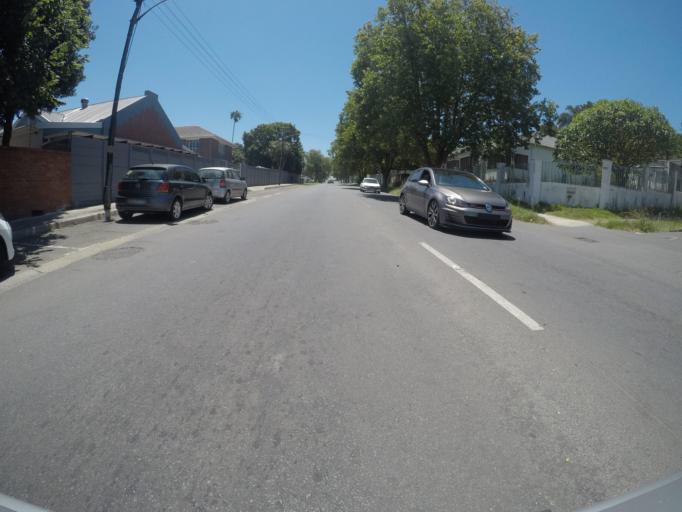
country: ZA
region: Eastern Cape
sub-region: Buffalo City Metropolitan Municipality
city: East London
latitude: -32.9885
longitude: 27.9018
